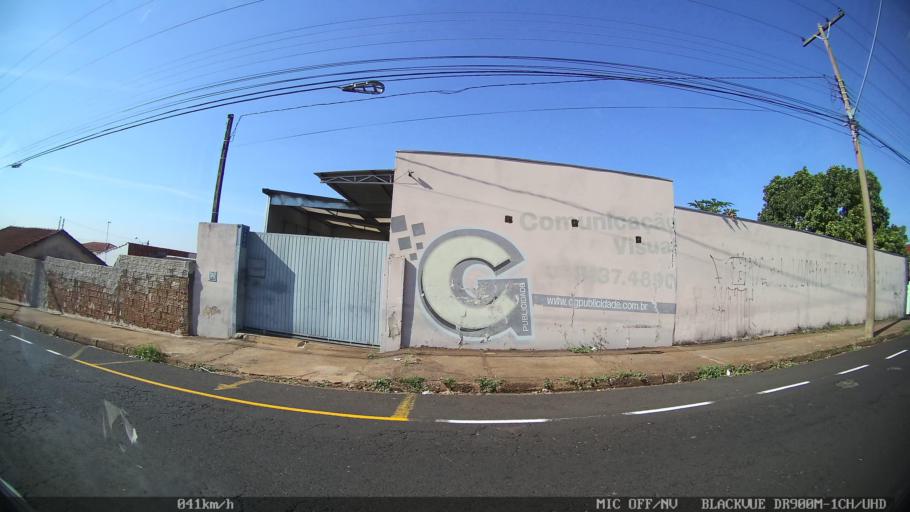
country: BR
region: Sao Paulo
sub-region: Sao Jose Do Rio Preto
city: Sao Jose do Rio Preto
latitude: -20.7775
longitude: -49.4003
